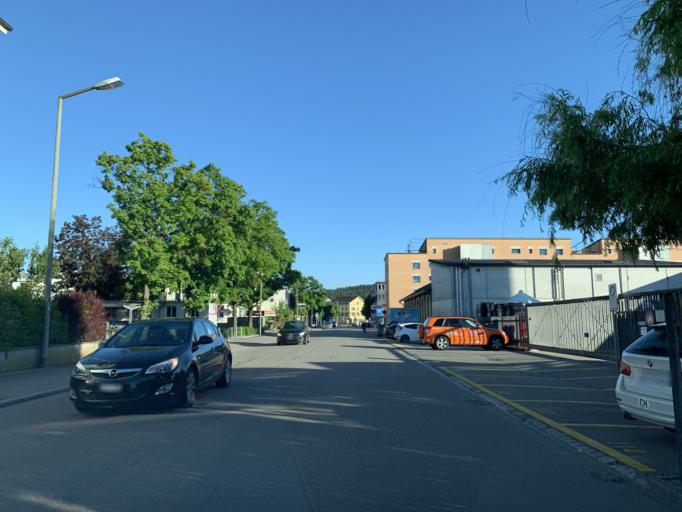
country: CH
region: Zurich
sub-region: Bezirk Winterthur
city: Mattenbach (Kreis 7) / Deutweg
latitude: 47.4961
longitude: 8.7405
